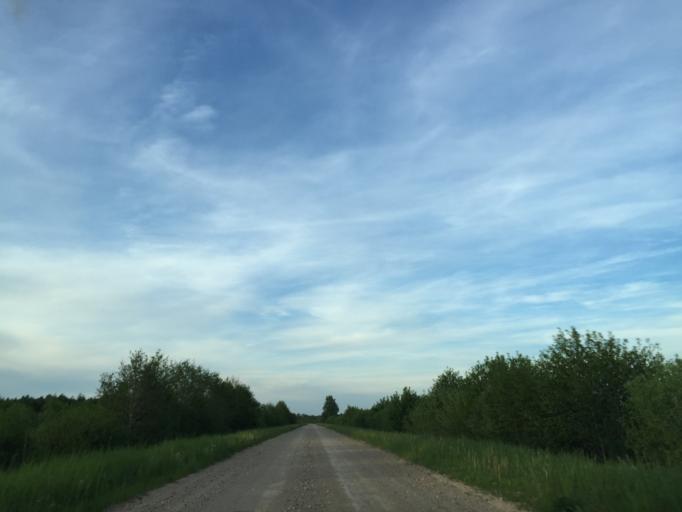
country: LV
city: Tireli
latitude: 56.7377
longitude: 23.5121
